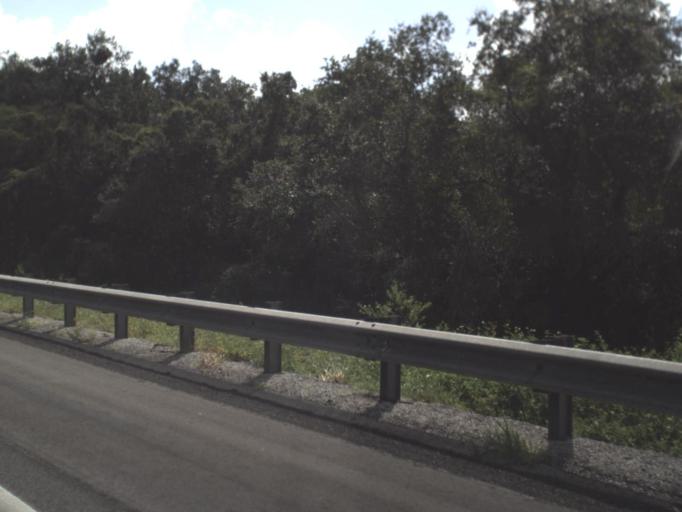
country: US
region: Florida
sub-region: Pasco County
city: San Antonio
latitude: 28.4027
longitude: -82.3093
